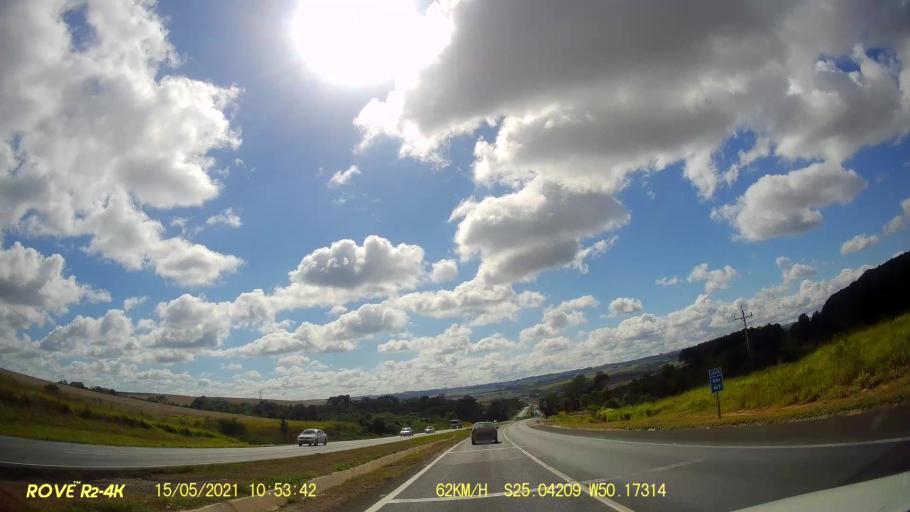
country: BR
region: Parana
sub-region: Ponta Grossa
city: Ponta Grossa
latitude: -25.0421
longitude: -50.1735
